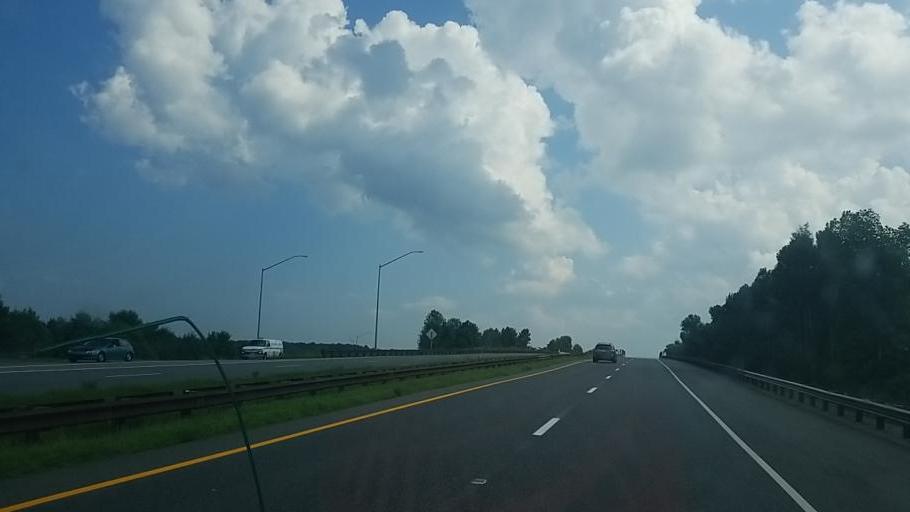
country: US
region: Maryland
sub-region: Worcester County
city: Ocean Pines
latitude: 38.3929
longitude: -75.2039
